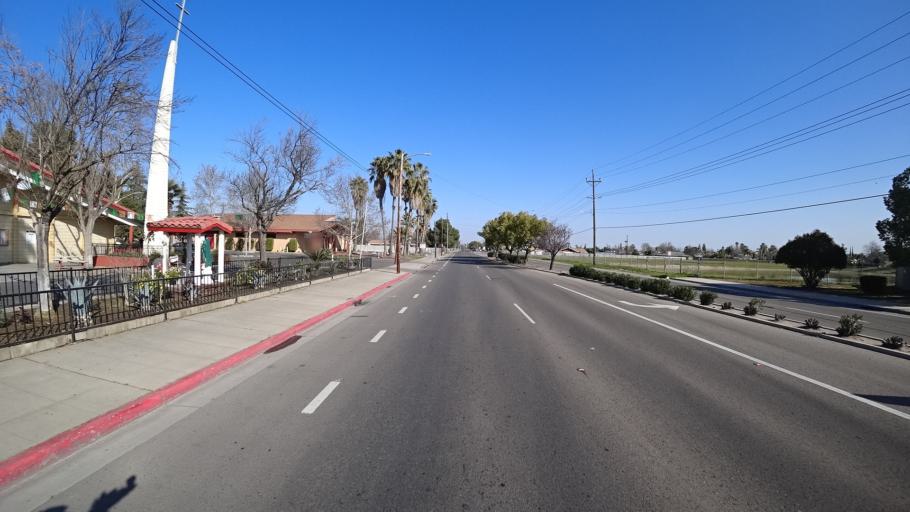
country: US
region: California
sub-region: Fresno County
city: Fresno
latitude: 36.7110
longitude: -119.7366
